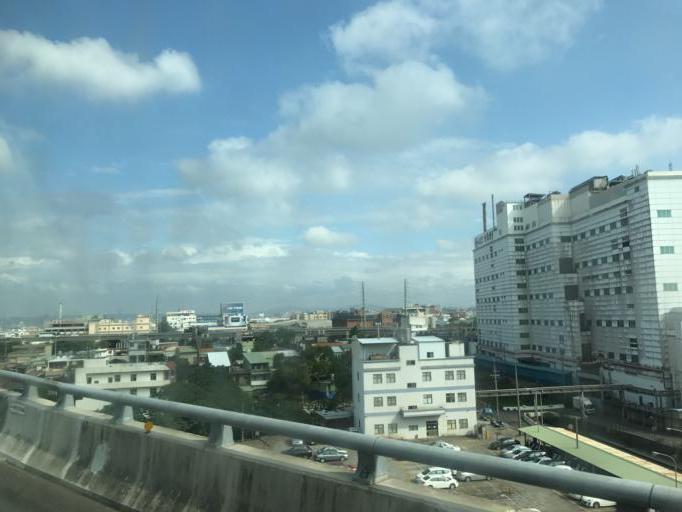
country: TW
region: Taiwan
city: Taoyuan City
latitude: 24.9862
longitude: 121.2355
